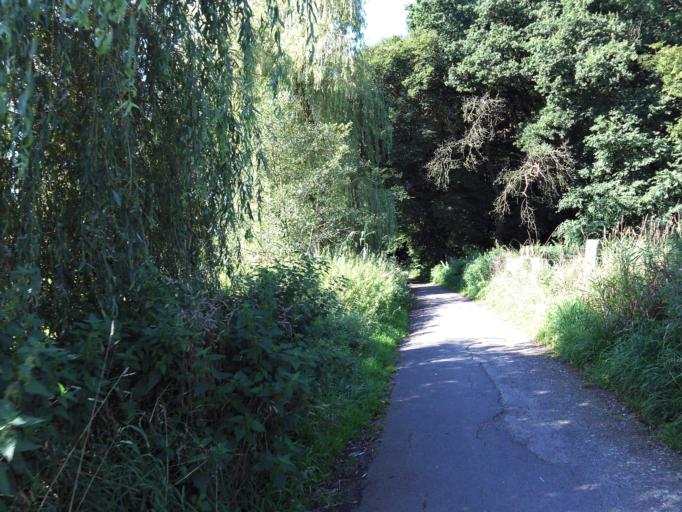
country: DE
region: North Rhine-Westphalia
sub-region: Regierungsbezirk Koln
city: Alsdorf
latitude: 50.8545
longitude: 6.1817
